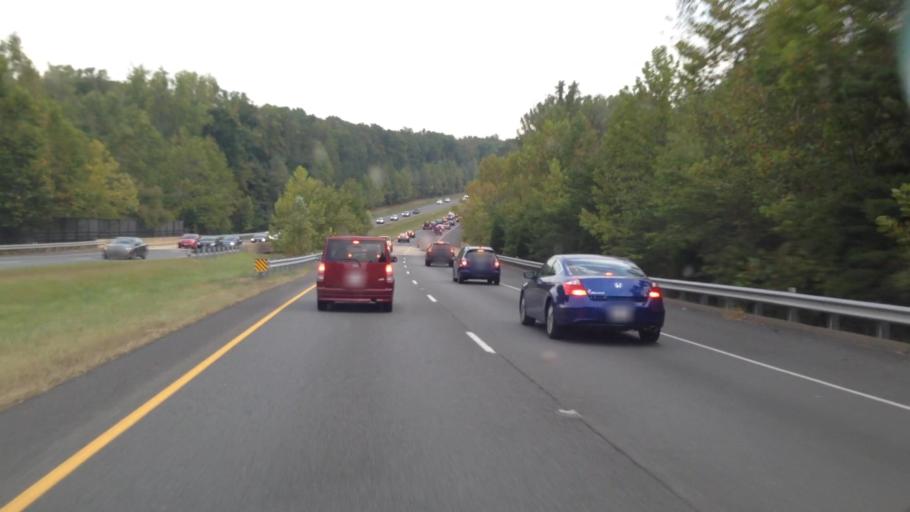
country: US
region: Virginia
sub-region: Fairfax County
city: Fairfax Station
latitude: 38.8027
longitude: -77.3424
